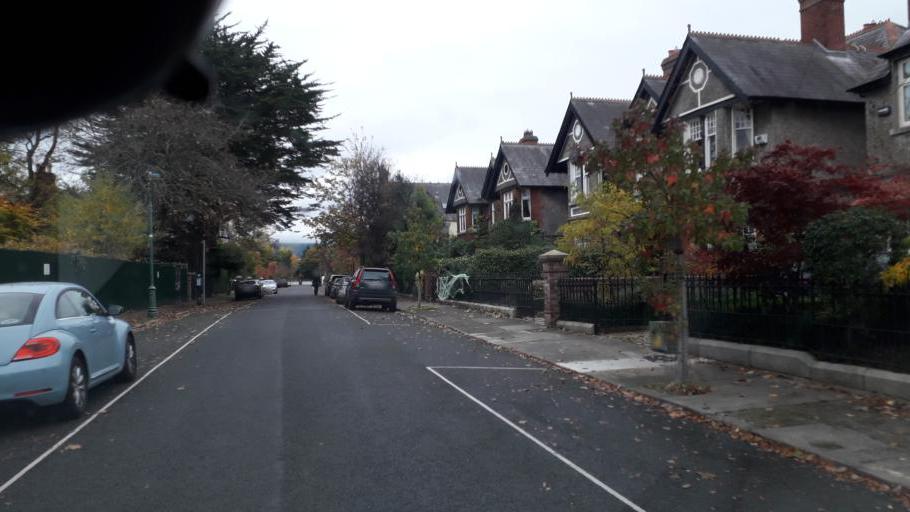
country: IE
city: Milltown
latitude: 53.3172
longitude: -6.2514
